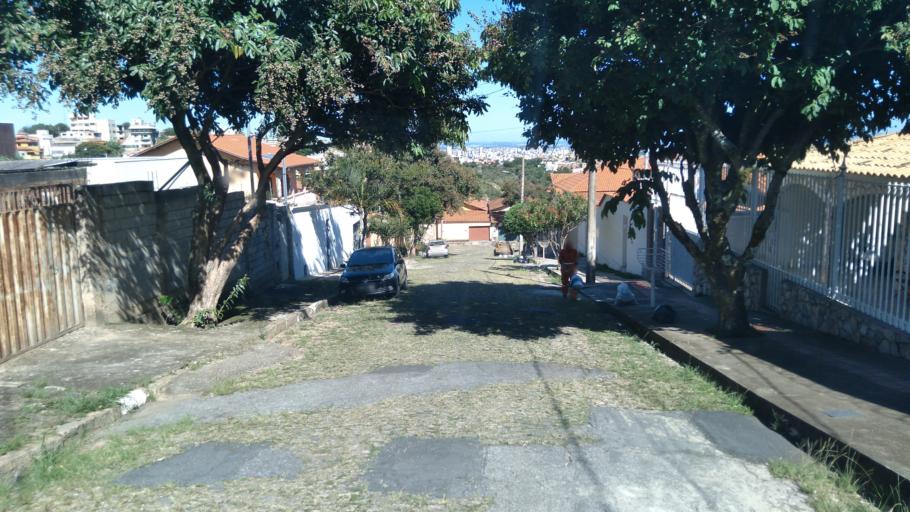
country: BR
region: Minas Gerais
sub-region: Belo Horizonte
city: Belo Horizonte
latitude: -19.9260
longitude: -43.8873
